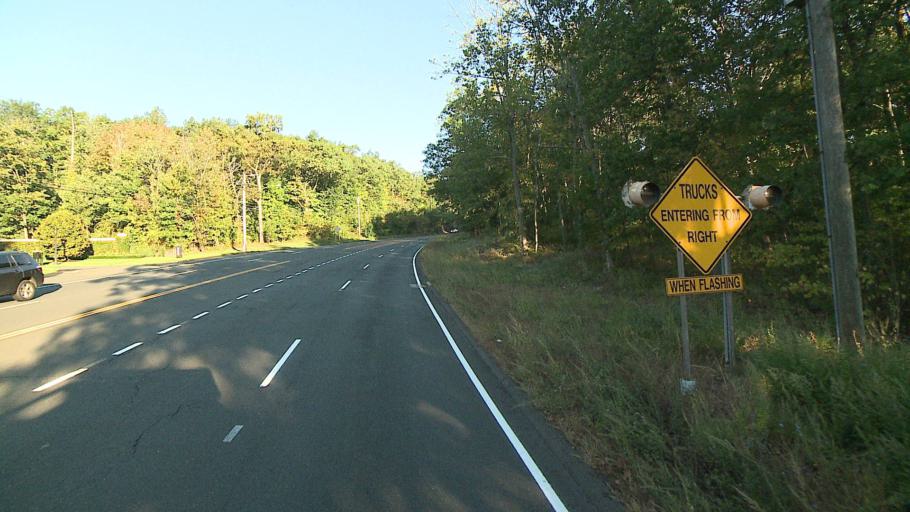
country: US
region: Connecticut
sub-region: Hartford County
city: Weatogue
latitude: 41.7939
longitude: -72.7956
